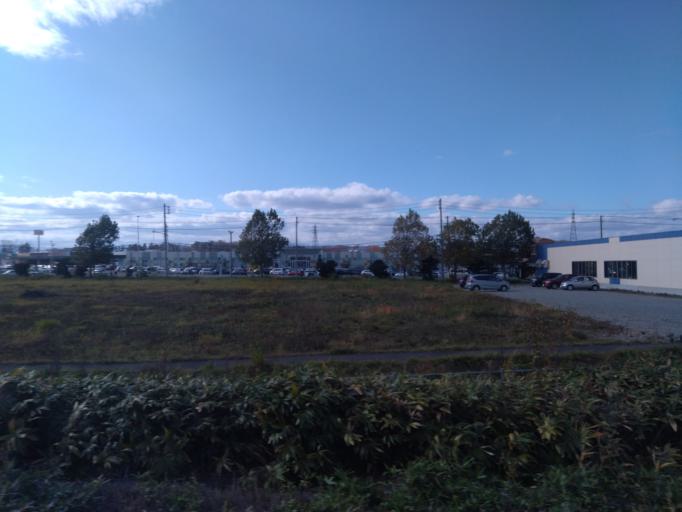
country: JP
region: Hokkaido
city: Kitahiroshima
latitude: 42.9057
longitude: 141.5743
